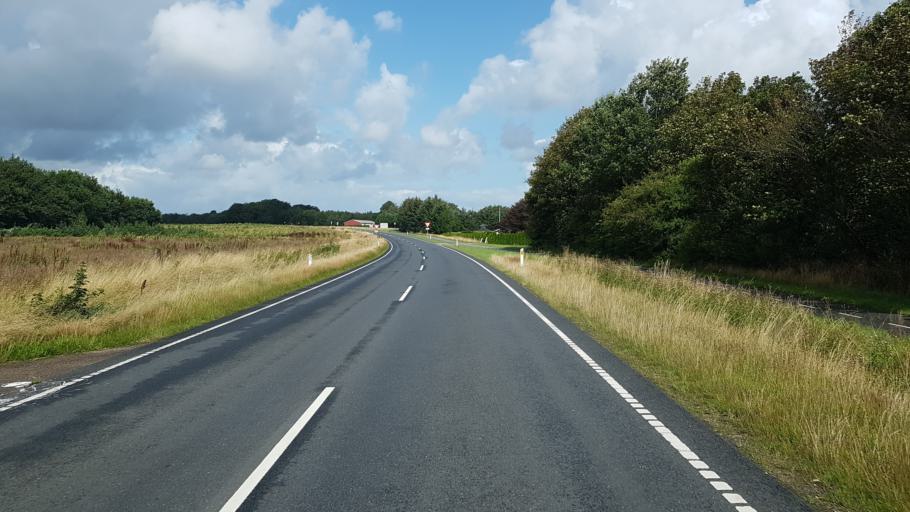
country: DK
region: South Denmark
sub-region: Vejen Kommune
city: Vejen
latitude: 55.5495
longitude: 9.1137
